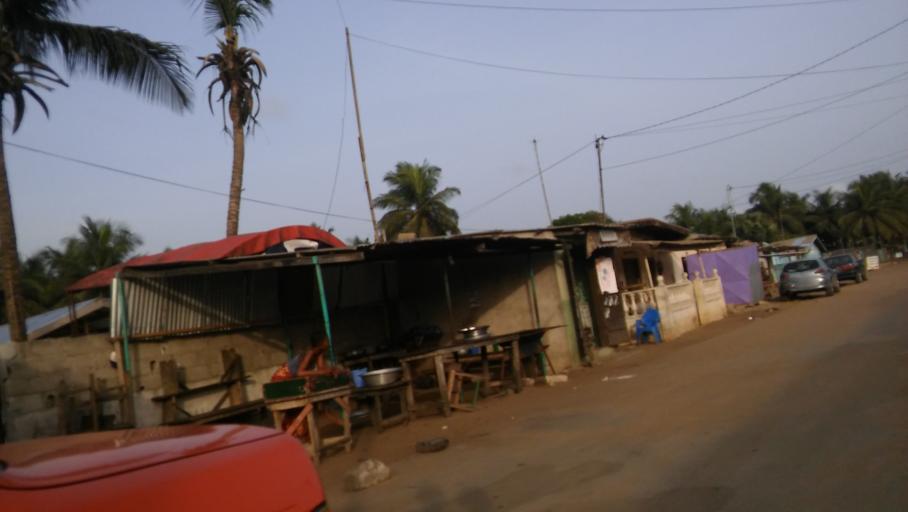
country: CI
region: Sud-Comoe
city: Grand-Bassam
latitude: 5.1942
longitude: -3.7261
